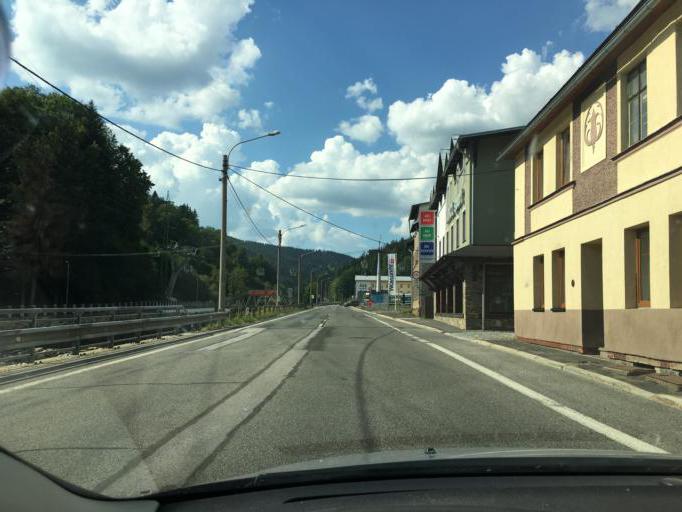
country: CZ
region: Kralovehradecky
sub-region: Okres Trutnov
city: Vrchlabi
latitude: 50.6524
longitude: 15.6048
